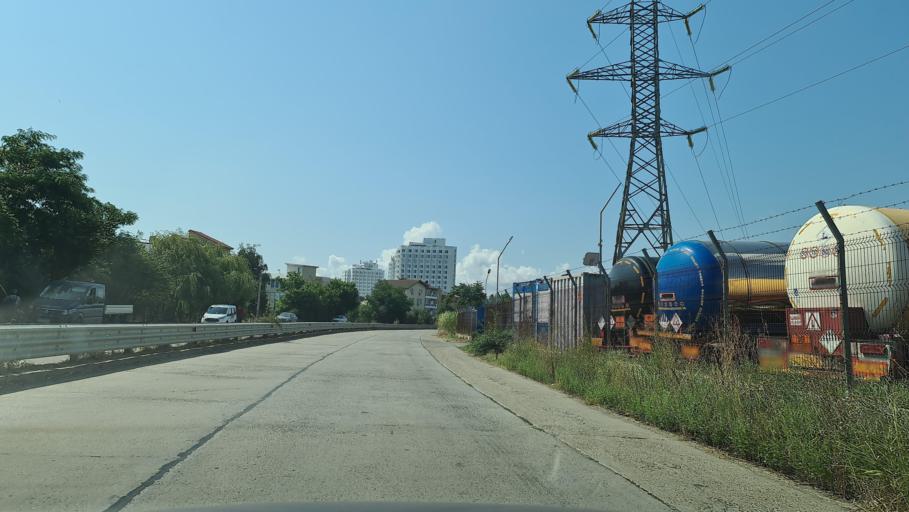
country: RO
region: Constanta
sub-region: Oras Eforie
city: Eforie Nord
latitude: 44.0797
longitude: 28.6385
